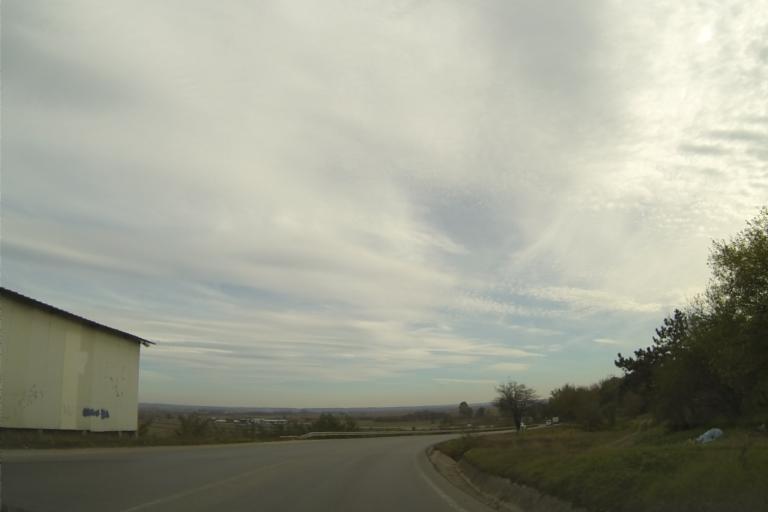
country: RO
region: Olt
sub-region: Comuna Ganeasa
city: Ganeasa
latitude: 44.4022
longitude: 24.2843
